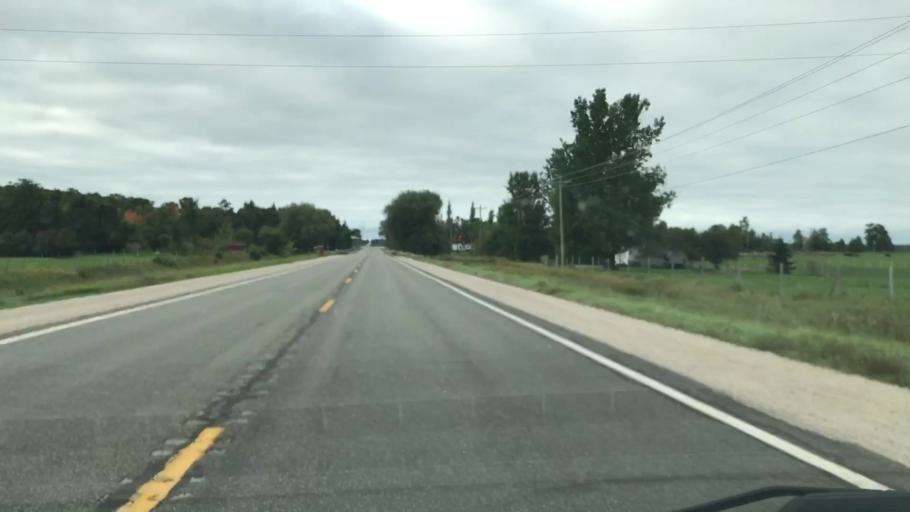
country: US
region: Michigan
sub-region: Luce County
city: Newberry
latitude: 46.1588
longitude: -85.5713
